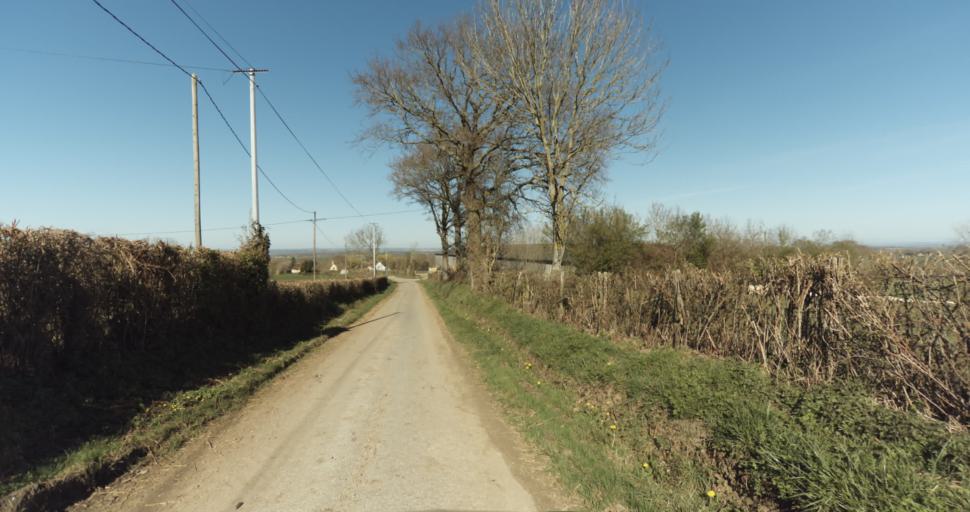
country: FR
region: Lower Normandy
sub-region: Departement de l'Orne
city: Trun
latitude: 48.9131
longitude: 0.0513
